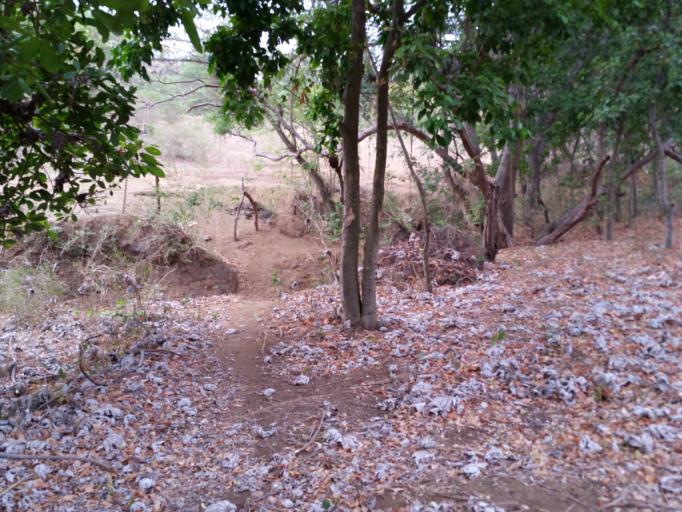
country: NI
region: Managua
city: Managua
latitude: 12.0883
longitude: -86.2491
